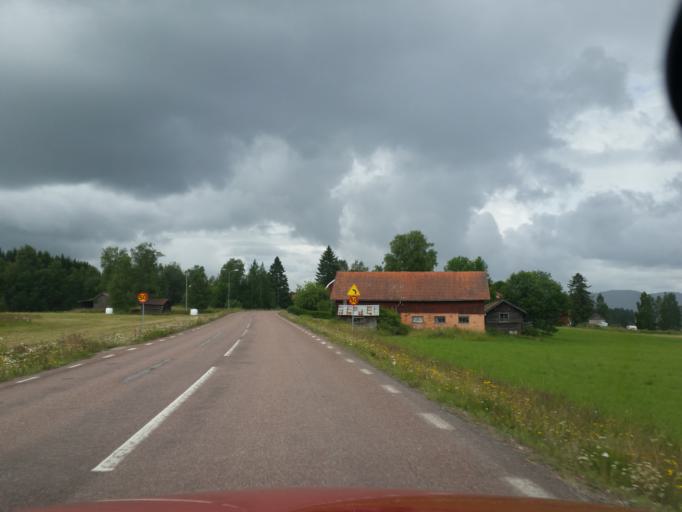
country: SE
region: Dalarna
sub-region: Gagnefs Kommun
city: Gagnef
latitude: 60.6704
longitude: 15.1472
